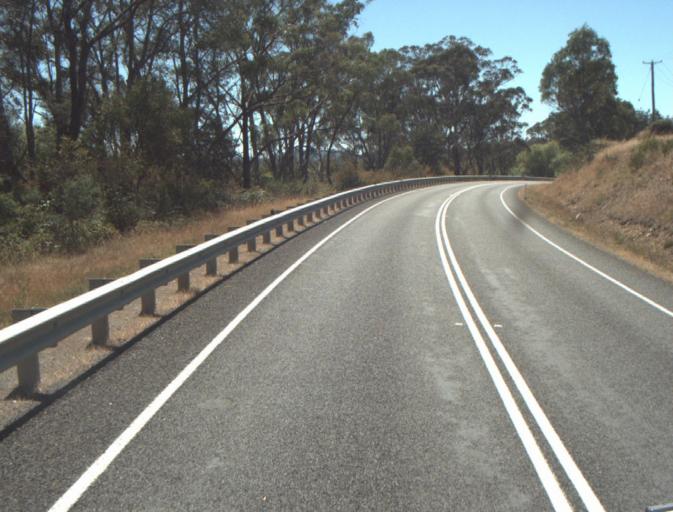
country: AU
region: Tasmania
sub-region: Launceston
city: Newstead
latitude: -41.3732
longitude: 147.3143
